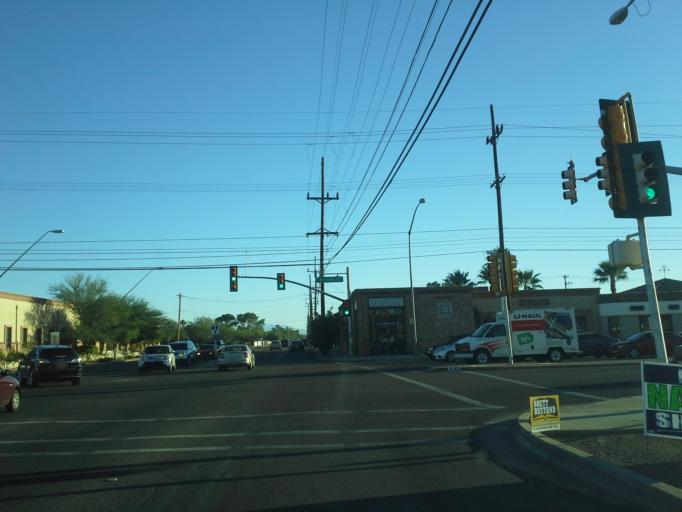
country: US
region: Arizona
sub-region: Pima County
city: Tucson
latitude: 32.2219
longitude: -110.9267
